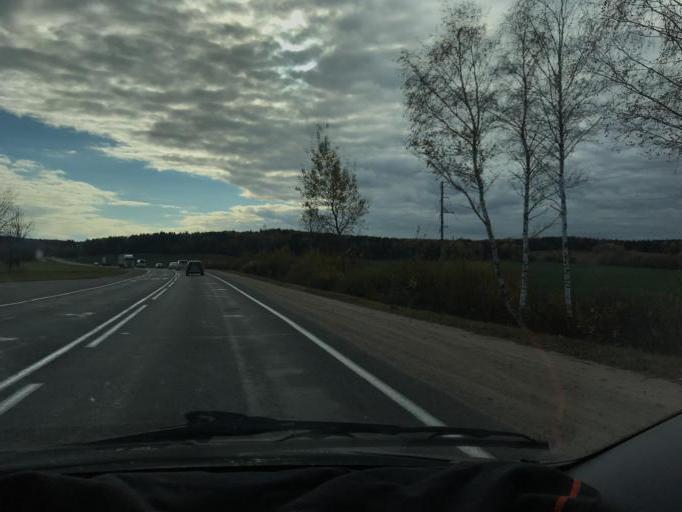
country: BY
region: Minsk
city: Lahoysk
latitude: 54.2325
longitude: 27.8363
